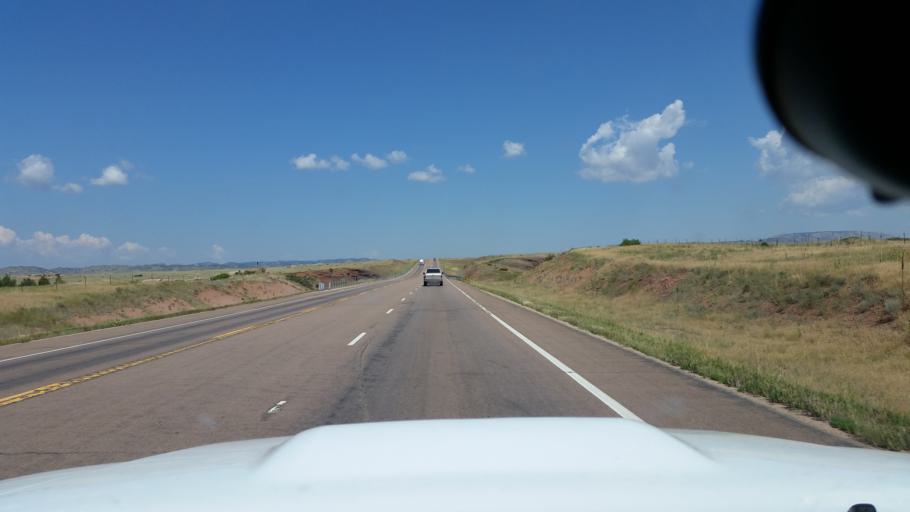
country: US
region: Colorado
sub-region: Larimer County
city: Laporte
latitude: 40.8947
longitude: -105.2940
